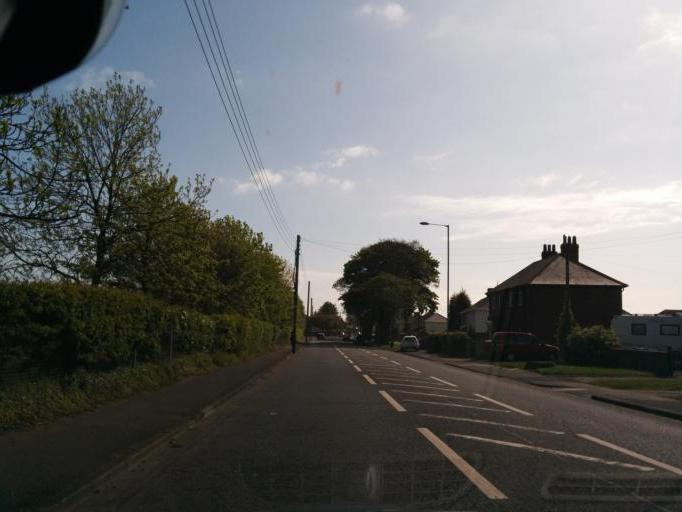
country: GB
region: England
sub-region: Northumberland
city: Ashington
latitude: 55.1621
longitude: -1.5921
